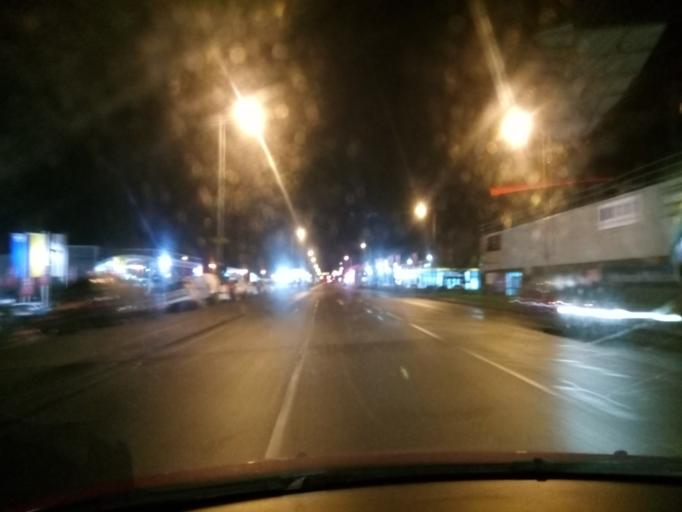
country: GB
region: Scotland
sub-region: West Lothian
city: Seafield
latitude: 55.9628
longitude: -3.1286
